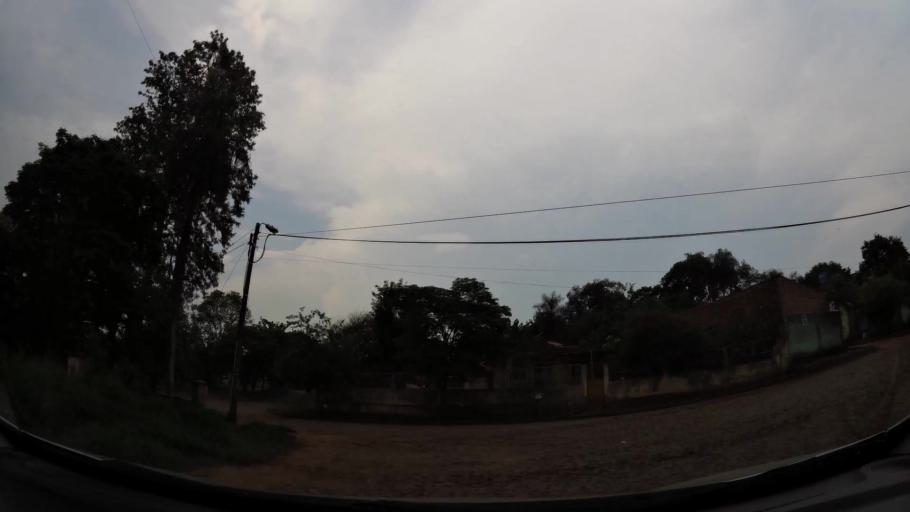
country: PY
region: Alto Parana
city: Presidente Franco
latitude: -25.5443
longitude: -54.6054
